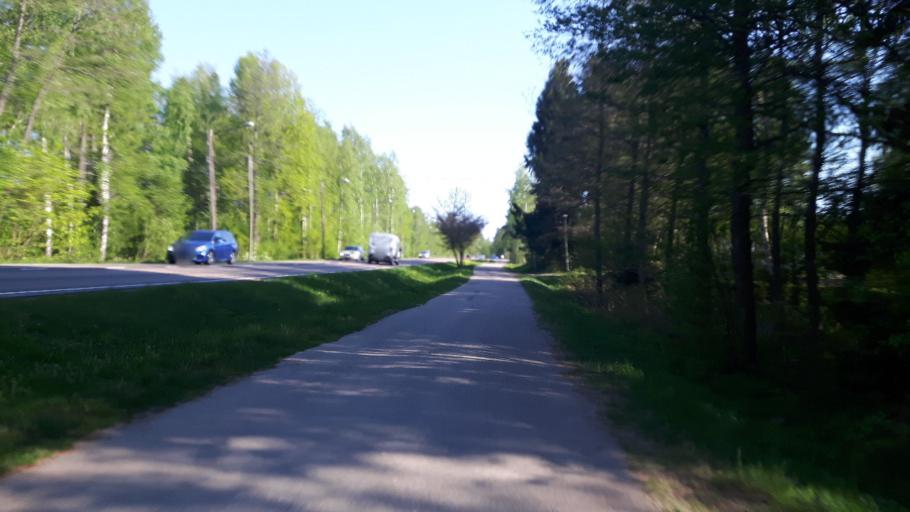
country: FI
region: Kymenlaakso
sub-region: Kotka-Hamina
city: Kotka
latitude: 60.4598
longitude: 26.8863
